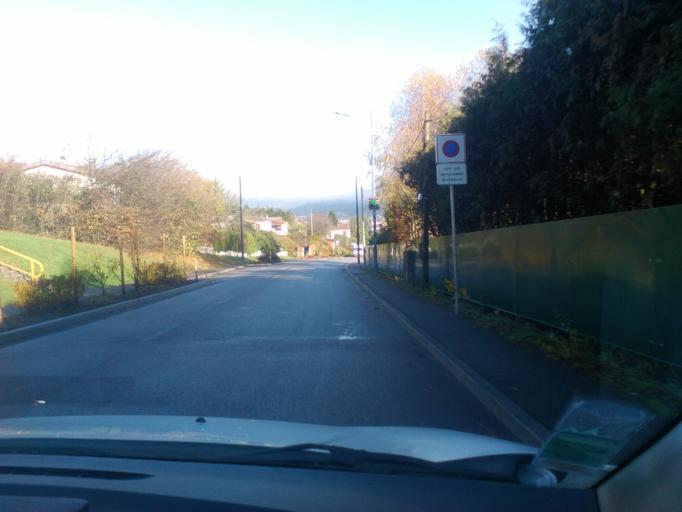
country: FR
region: Lorraine
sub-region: Departement des Vosges
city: Remiremont
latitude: 48.0082
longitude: 6.5813
